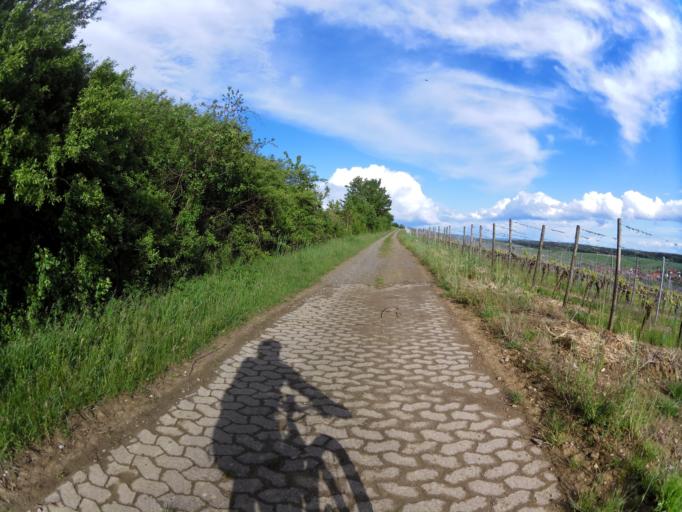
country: DE
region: Bavaria
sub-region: Regierungsbezirk Unterfranken
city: Volkach
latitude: 49.8806
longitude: 10.2554
